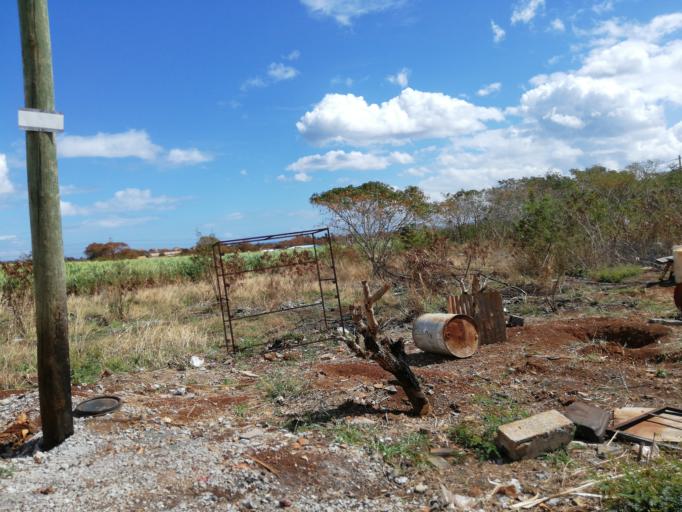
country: MU
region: Black River
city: Petite Riviere
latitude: -20.1948
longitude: 57.4630
